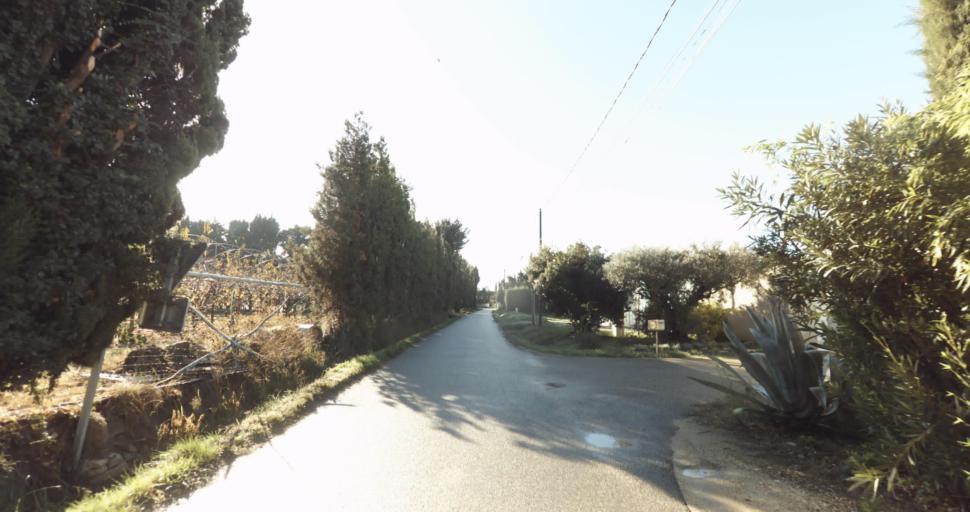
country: FR
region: Provence-Alpes-Cote d'Azur
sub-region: Departement des Bouches-du-Rhone
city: Rognonas
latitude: 43.8902
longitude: 4.8029
